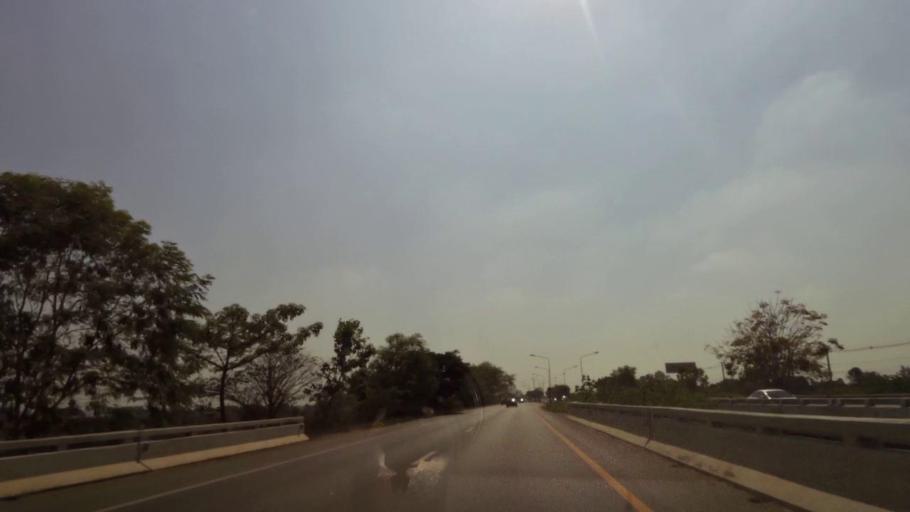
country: TH
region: Phichit
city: Wachira Barami
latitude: 16.4725
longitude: 100.1475
